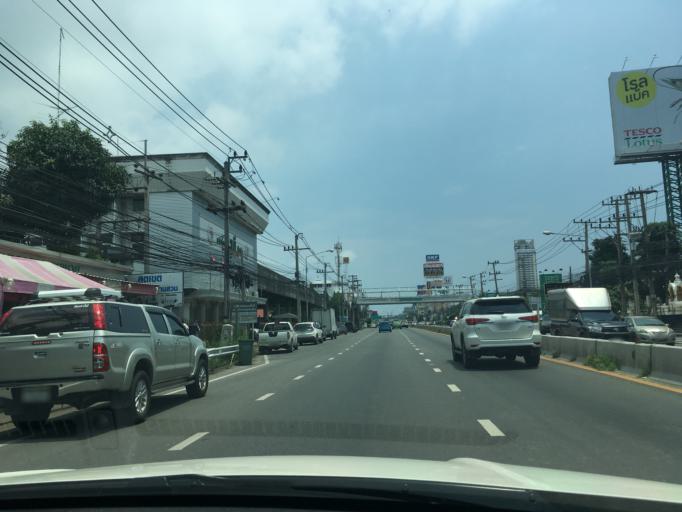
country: TH
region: Chon Buri
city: Chon Buri
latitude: 13.3407
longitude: 100.9741
